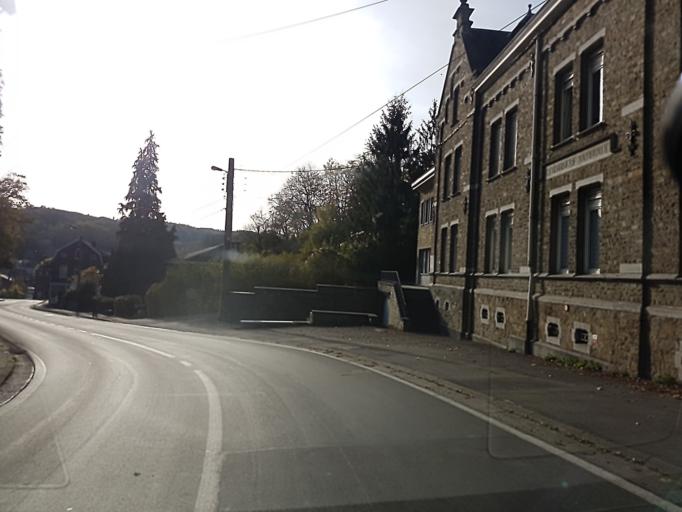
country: BE
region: Wallonia
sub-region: Province de Liege
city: Esneux
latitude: 50.5356
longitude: 5.5665
